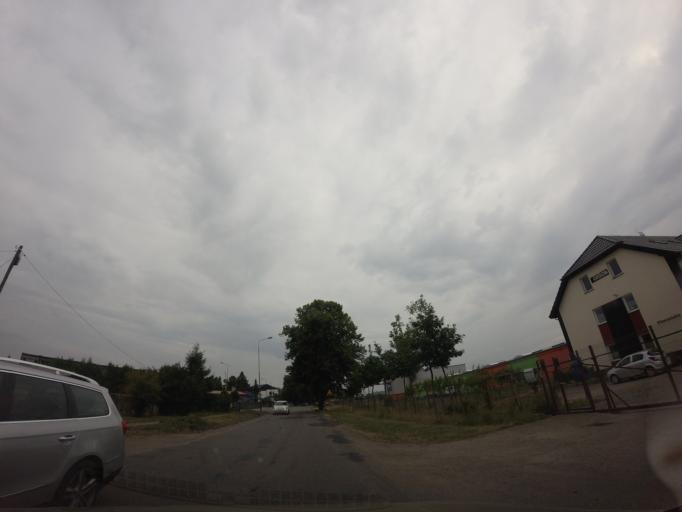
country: PL
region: West Pomeranian Voivodeship
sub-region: Powiat drawski
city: Czaplinek
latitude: 53.5500
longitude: 16.2323
